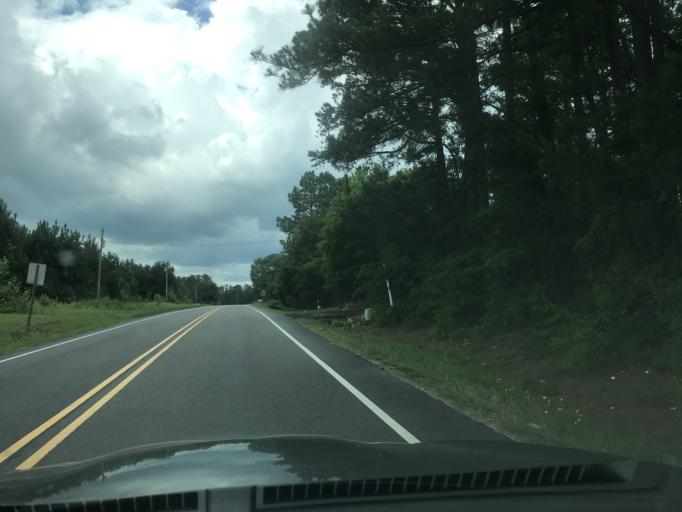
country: US
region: North Carolina
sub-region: Wake County
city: Knightdale
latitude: 35.8334
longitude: -78.4704
